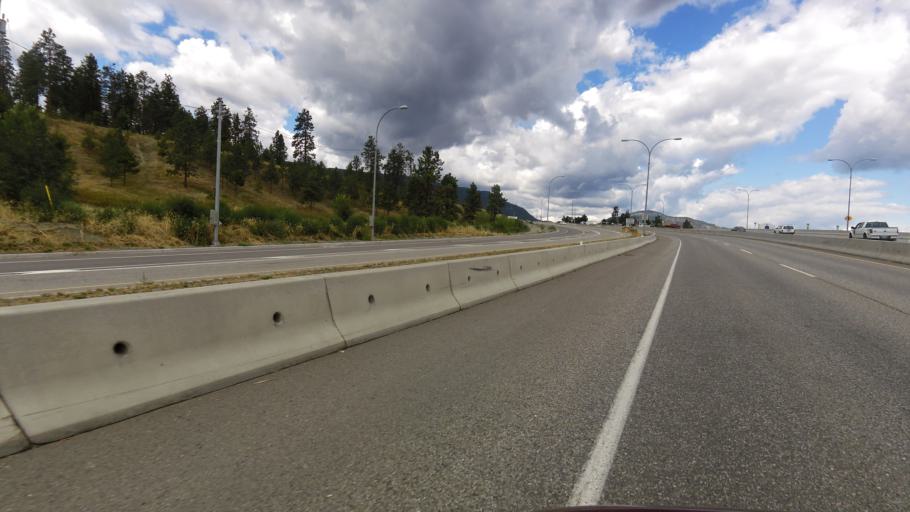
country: CA
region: British Columbia
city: Kelowna
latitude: 49.8807
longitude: -119.5242
